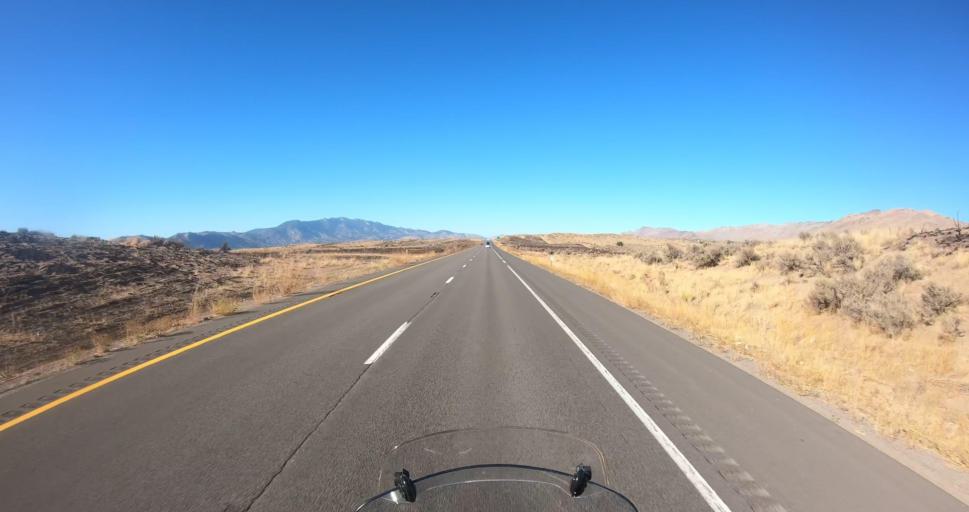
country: US
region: Nevada
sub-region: Washoe County
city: Cold Springs
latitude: 39.7517
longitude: -120.0379
